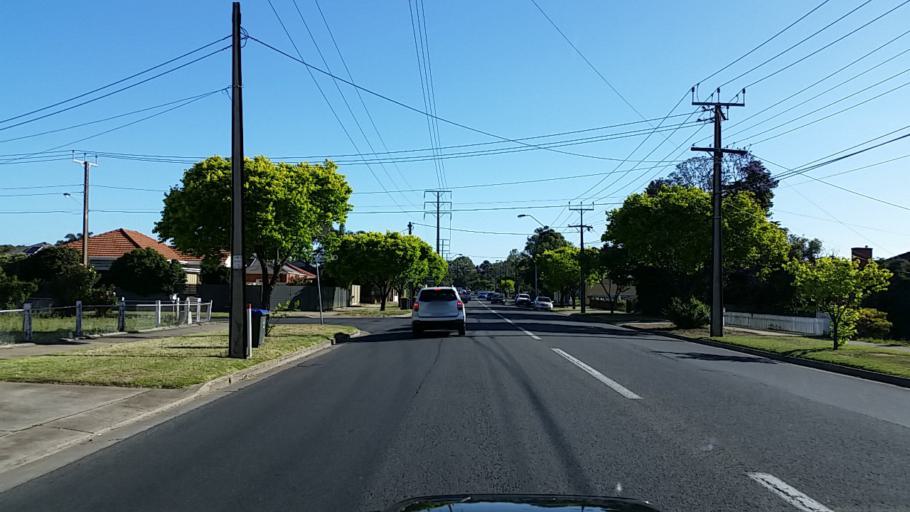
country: AU
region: South Australia
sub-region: Charles Sturt
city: Allenby Gardens
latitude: -34.9096
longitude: 138.5494
